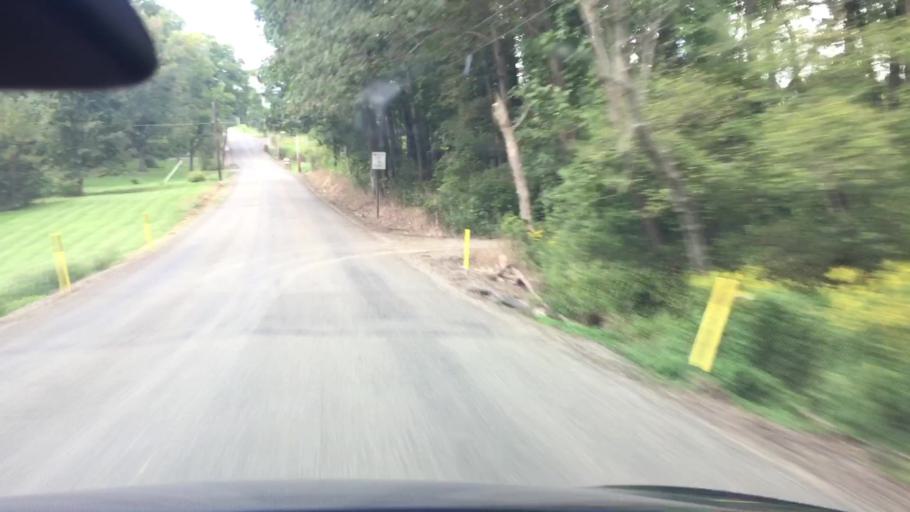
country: US
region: Pennsylvania
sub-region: Butler County
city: Meadowood
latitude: 40.8162
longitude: -79.8734
